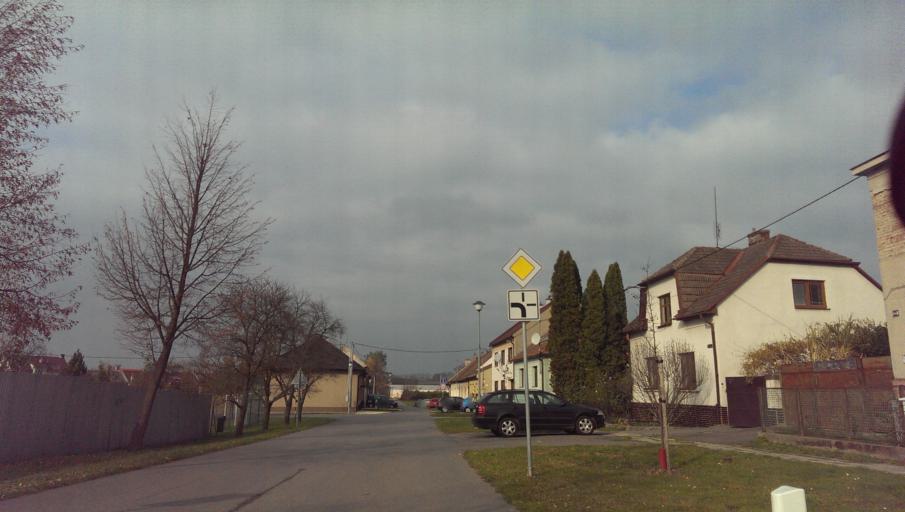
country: CZ
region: Zlin
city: Tlumacov
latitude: 49.2584
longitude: 17.5021
